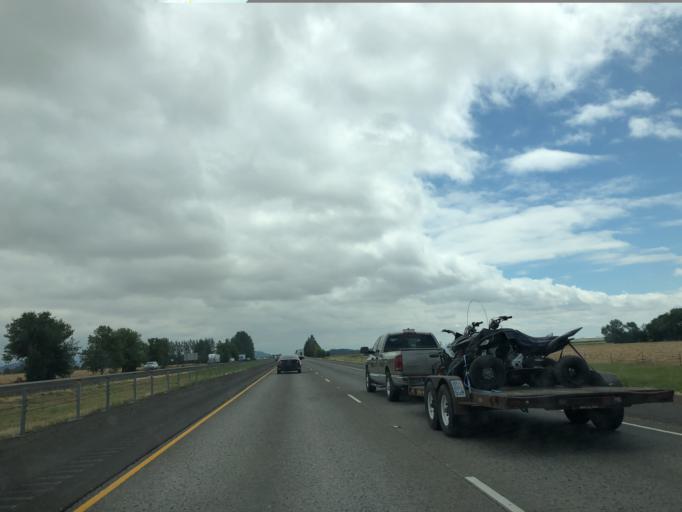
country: US
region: Oregon
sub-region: Linn County
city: Tangent
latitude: 44.5354
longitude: -123.0620
